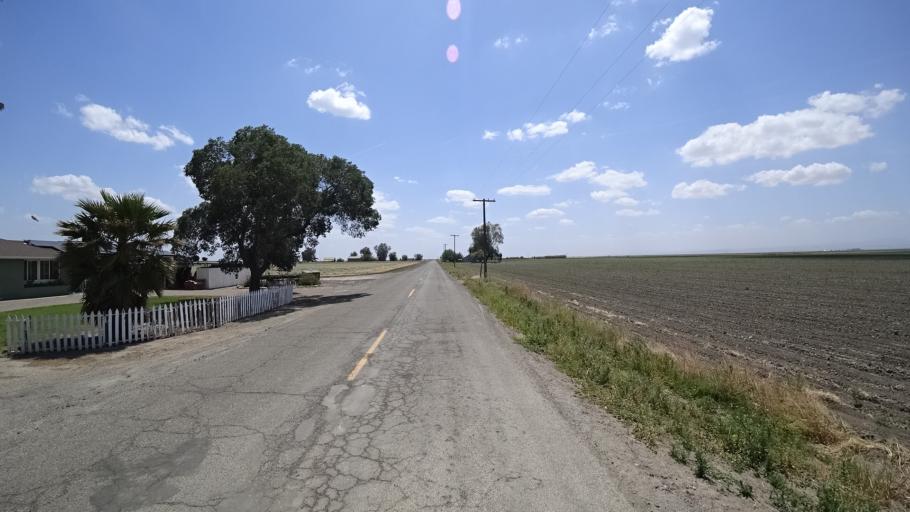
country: US
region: California
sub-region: Kings County
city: Stratford
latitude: 36.1598
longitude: -119.8160
